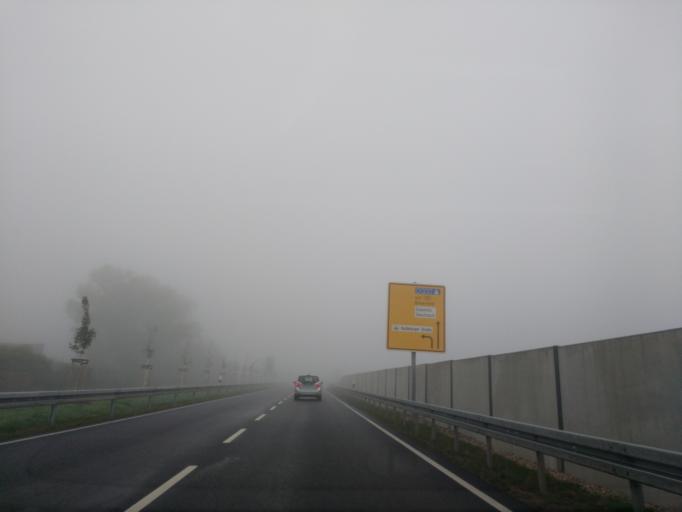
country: DE
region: Saxony-Anhalt
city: Halle (Saale)
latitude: 51.4816
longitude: 12.0183
